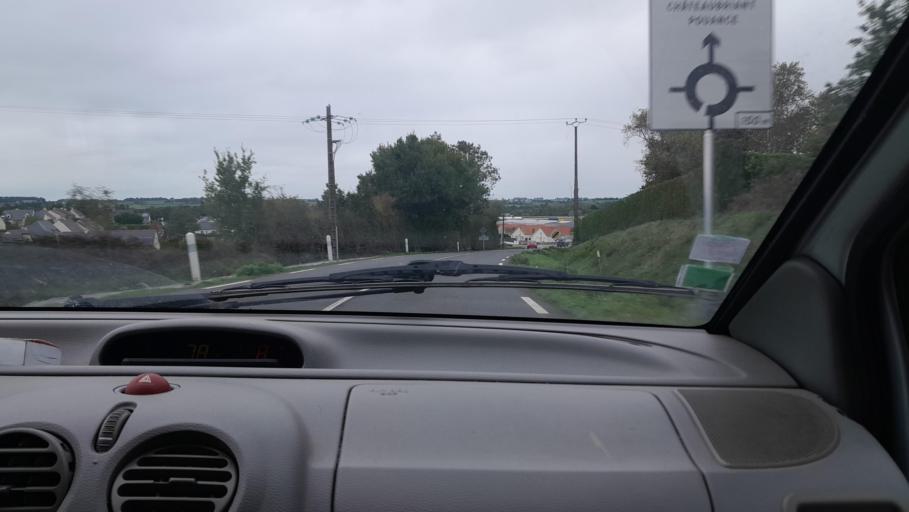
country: FR
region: Pays de la Loire
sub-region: Departement de la Loire-Atlantique
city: Saint-Mars-la-Jaille
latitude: 47.5133
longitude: -1.1845
